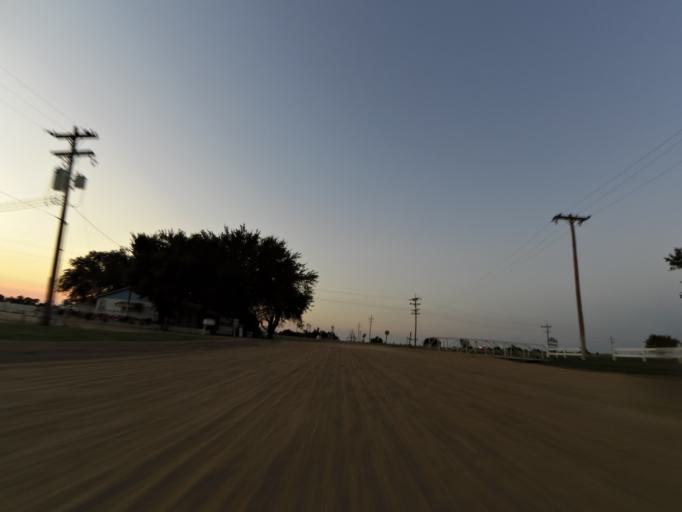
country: US
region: Kansas
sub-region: Reno County
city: South Hutchinson
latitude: 37.9962
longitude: -98.0320
